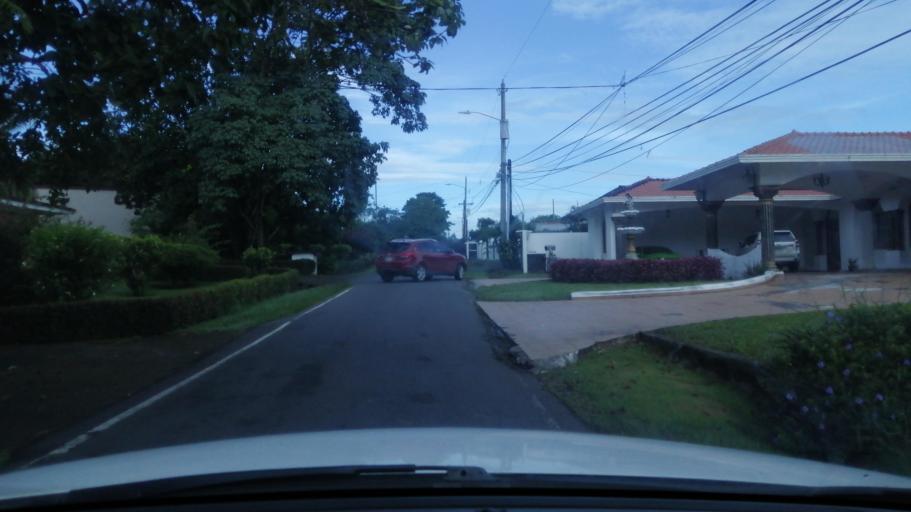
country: PA
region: Chiriqui
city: Mata del Nance
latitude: 8.4530
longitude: -82.4176
